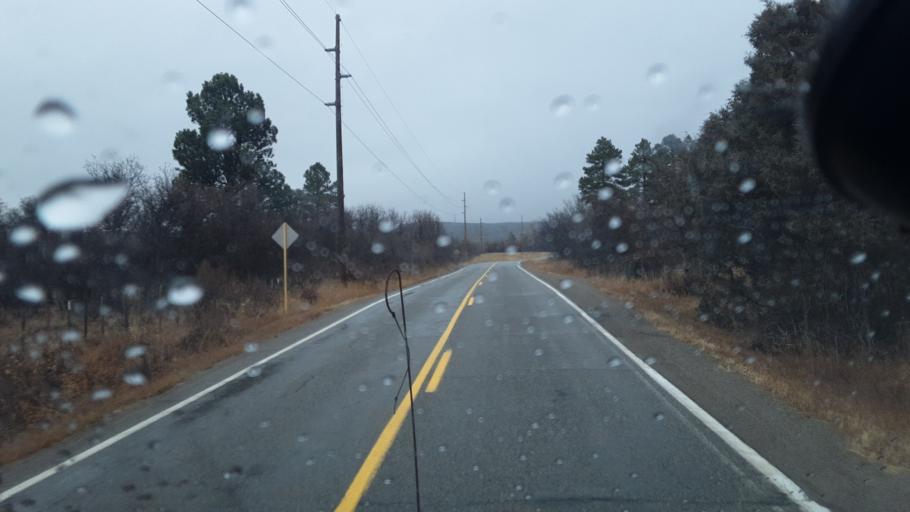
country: US
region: Colorado
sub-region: La Plata County
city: Durango
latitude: 37.2514
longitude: -108.0357
